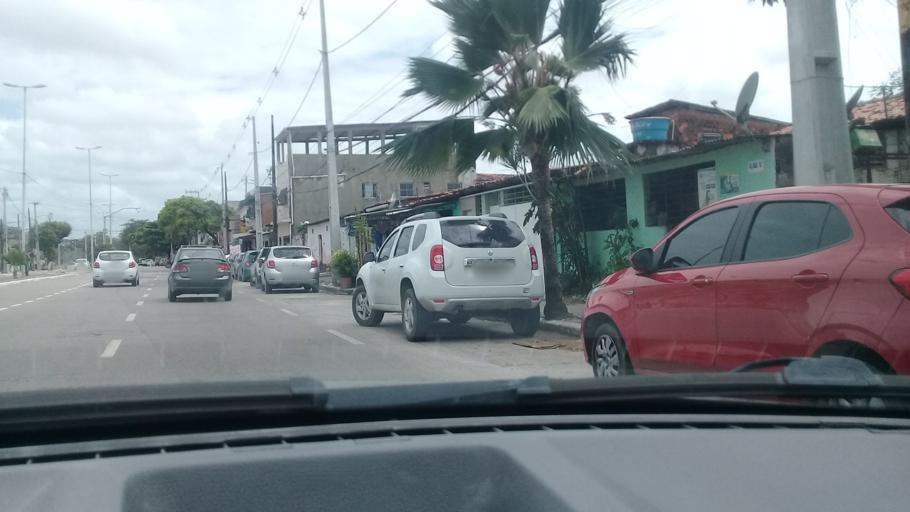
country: BR
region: Pernambuco
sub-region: Recife
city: Recife
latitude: -8.0423
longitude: -34.8769
